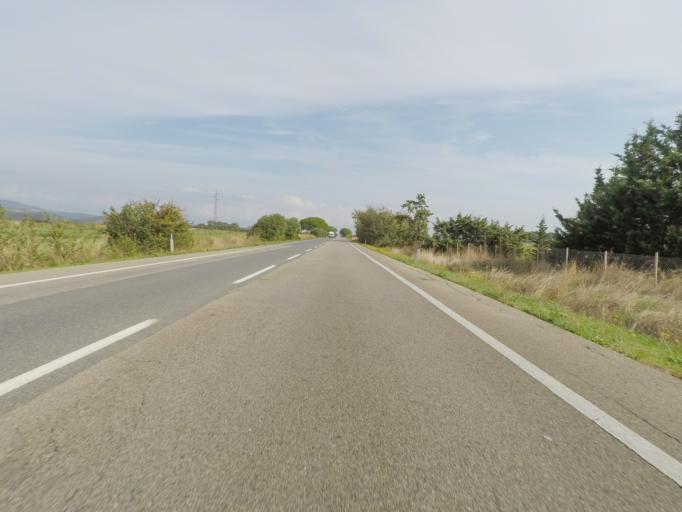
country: IT
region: Tuscany
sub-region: Provincia di Grosseto
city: Capalbio
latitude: 42.4152
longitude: 11.3574
